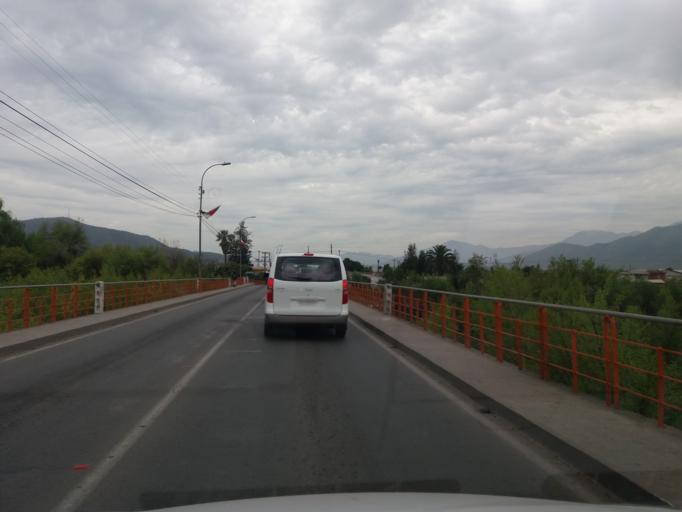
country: CL
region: Valparaiso
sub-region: Provincia de Quillota
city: Hacienda La Calera
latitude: -32.7795
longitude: -71.1912
